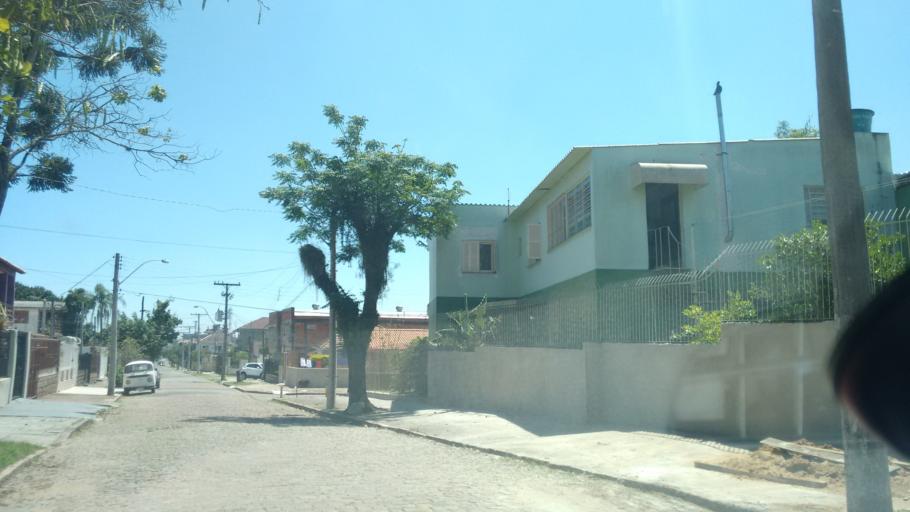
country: BR
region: Rio Grande do Sul
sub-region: Cachoeirinha
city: Cachoeirinha
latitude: -30.0006
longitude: -51.1289
